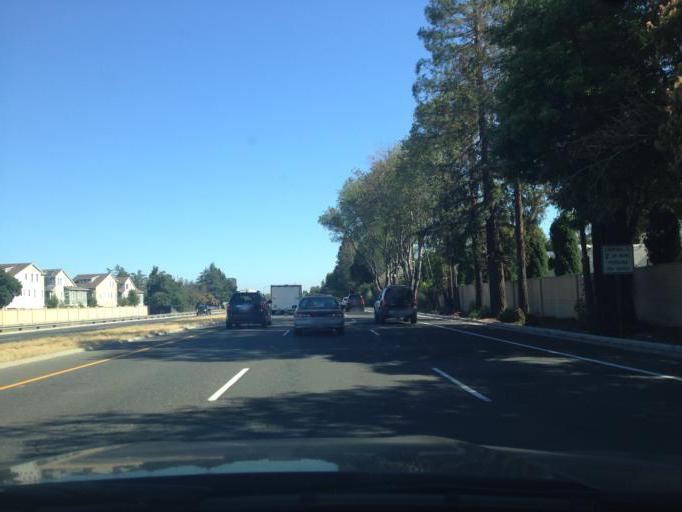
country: US
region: California
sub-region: Santa Clara County
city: Campbell
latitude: 37.2905
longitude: -121.9605
